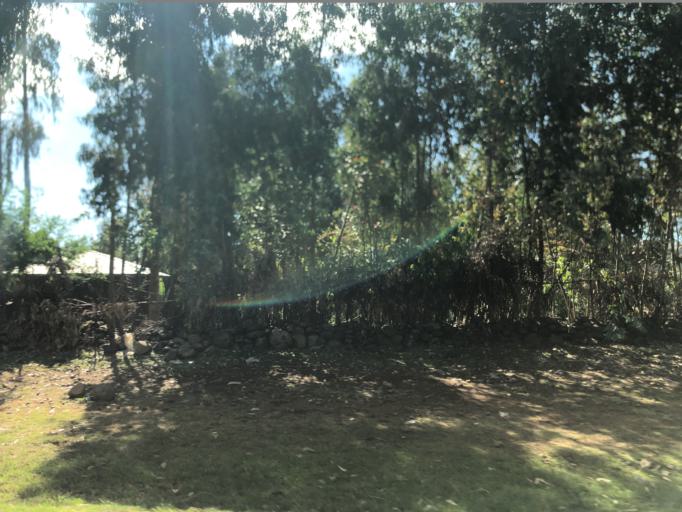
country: ET
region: Amhara
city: Debre Tabor
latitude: 11.7174
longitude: 38.4551
